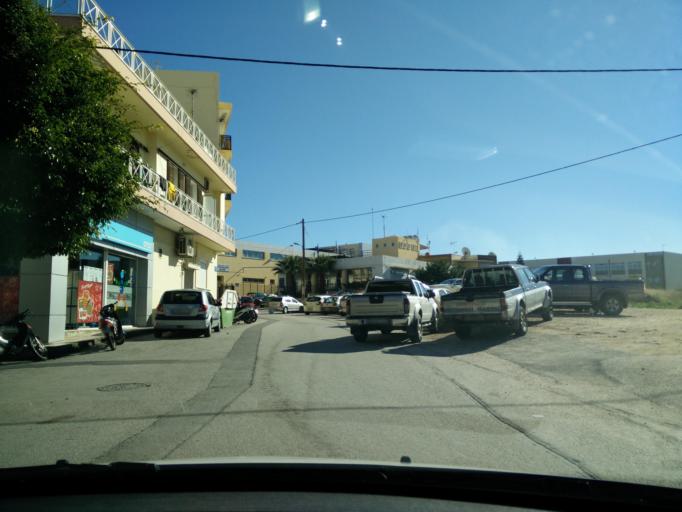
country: GR
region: Crete
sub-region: Nomos Irakleiou
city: Irakleion
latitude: 35.3280
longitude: 25.1429
